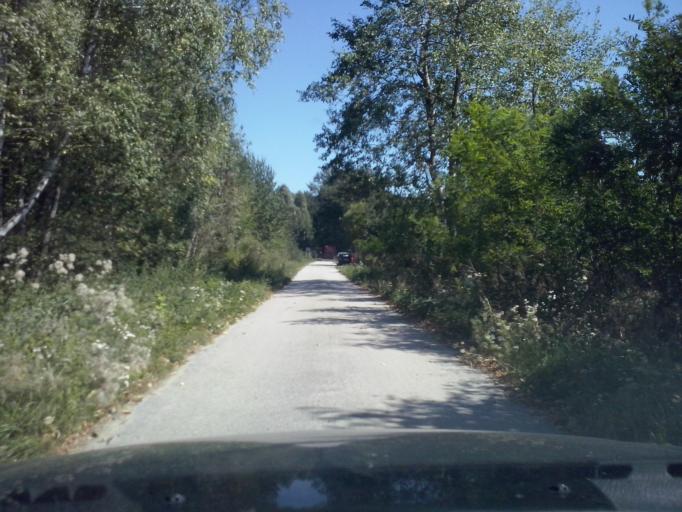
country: PL
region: Swietokrzyskie
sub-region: Powiat buski
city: Gnojno
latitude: 50.6088
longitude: 20.9276
